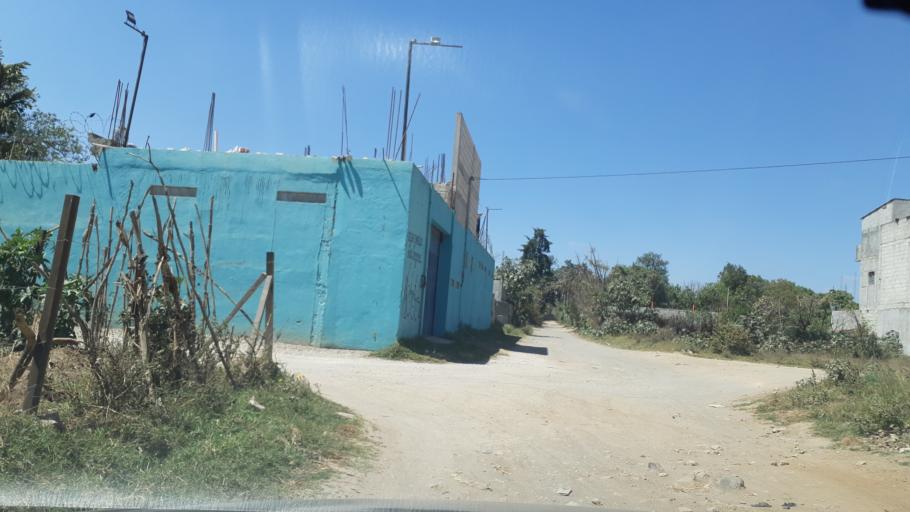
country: GT
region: Chimaltenango
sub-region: Municipio de Chimaltenango
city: Chimaltenango
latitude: 14.6477
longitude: -90.8098
